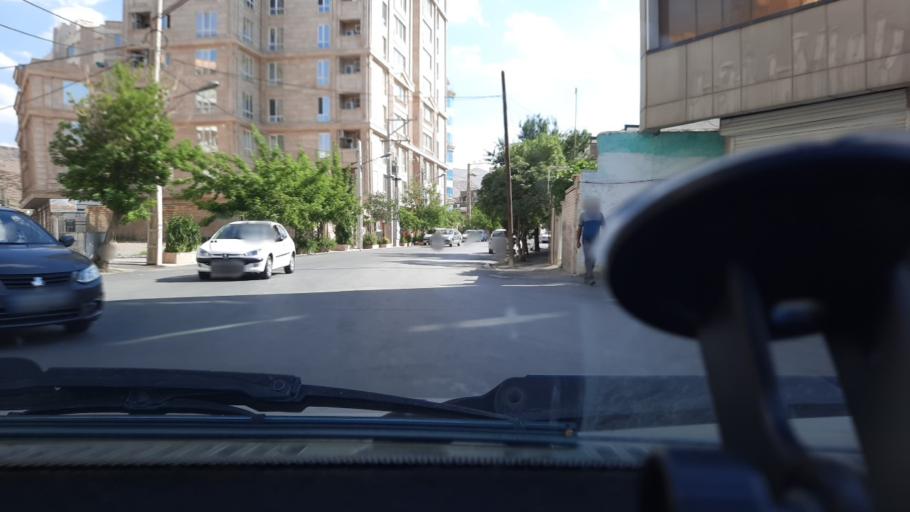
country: IR
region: Markazi
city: Arak
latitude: 34.0796
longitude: 49.6883
